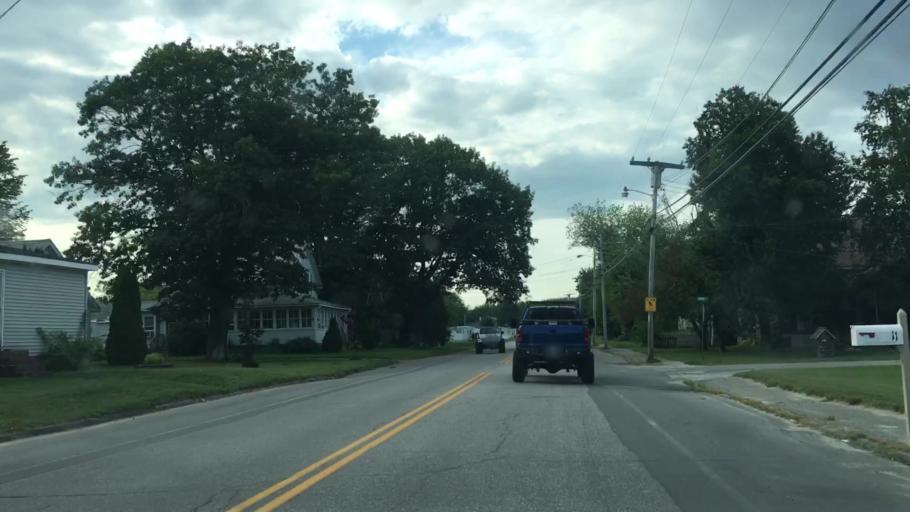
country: US
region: Maine
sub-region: Penobscot County
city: Howland
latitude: 45.2417
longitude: -68.6588
